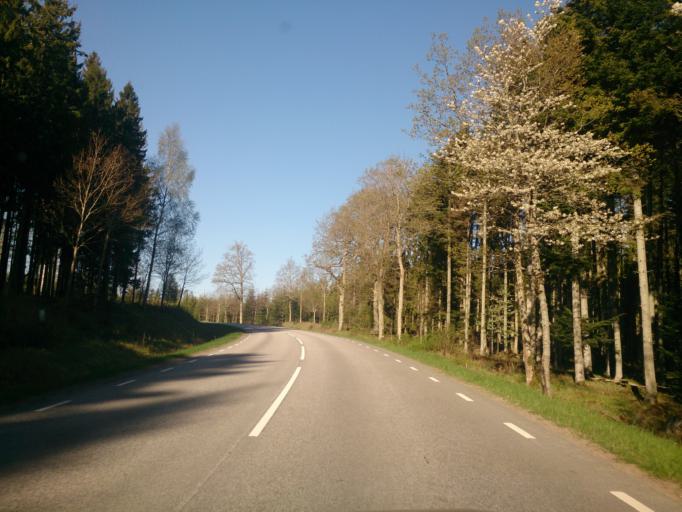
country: SE
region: OEstergoetland
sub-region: Linkopings Kommun
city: Berg
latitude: 58.5315
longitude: 15.5666
